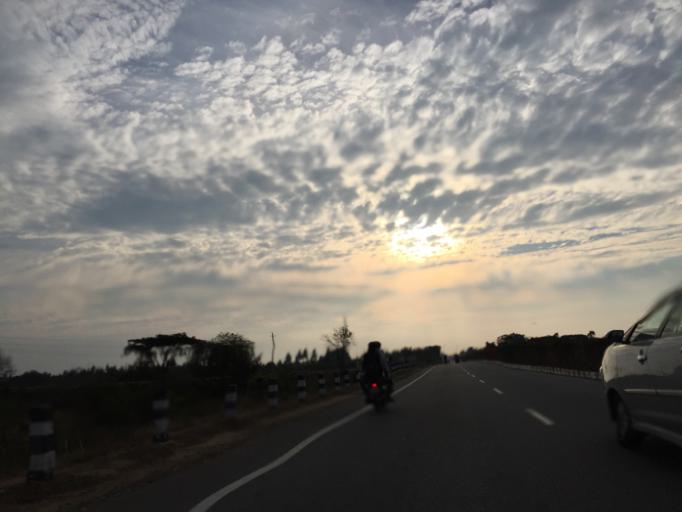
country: IN
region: Karnataka
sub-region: Kolar
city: Kolar
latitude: 13.1459
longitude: 78.2455
